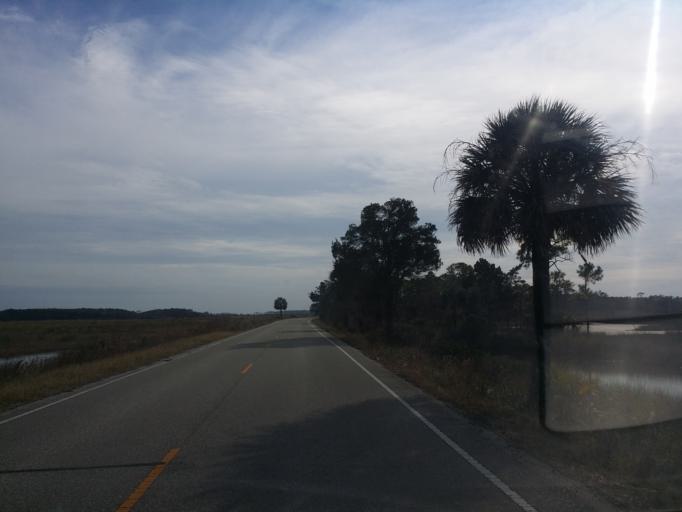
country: US
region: Florida
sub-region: Leon County
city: Woodville
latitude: 30.1204
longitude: -84.1481
